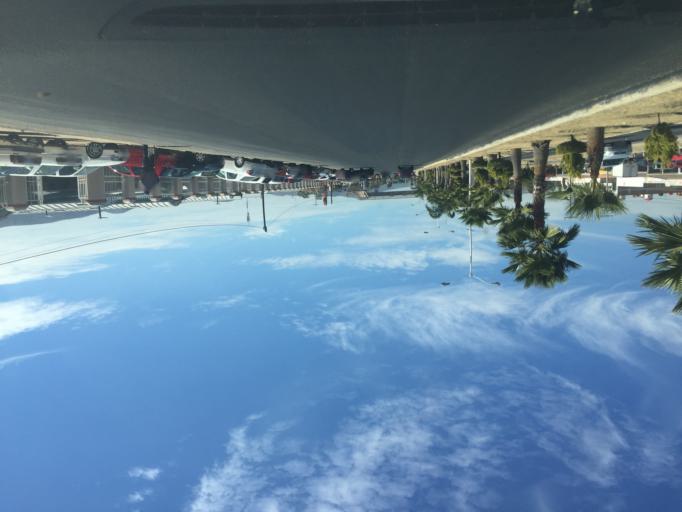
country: MX
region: Queretaro
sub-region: Tequisquiapan
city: Tequisquiapan
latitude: 20.5161
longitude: -99.9014
